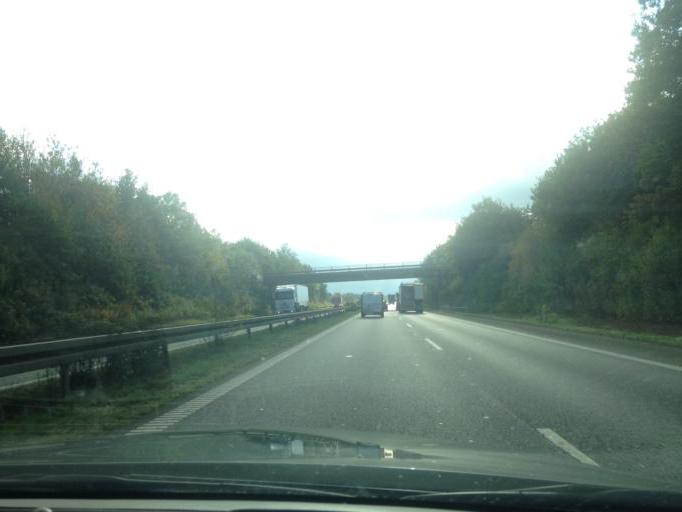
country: DK
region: South Denmark
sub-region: Fredericia Kommune
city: Taulov
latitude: 55.5866
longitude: 9.5797
